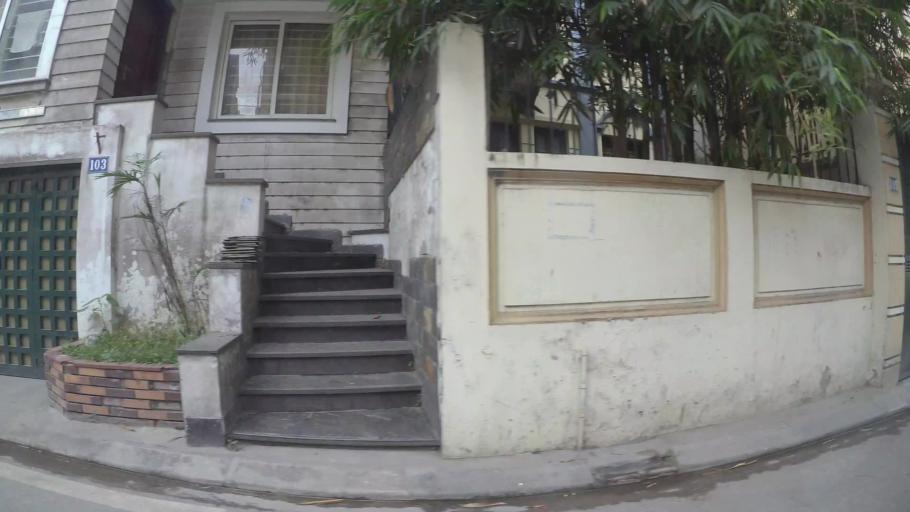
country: VN
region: Ha Noi
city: Tay Ho
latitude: 21.0598
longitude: 105.8367
